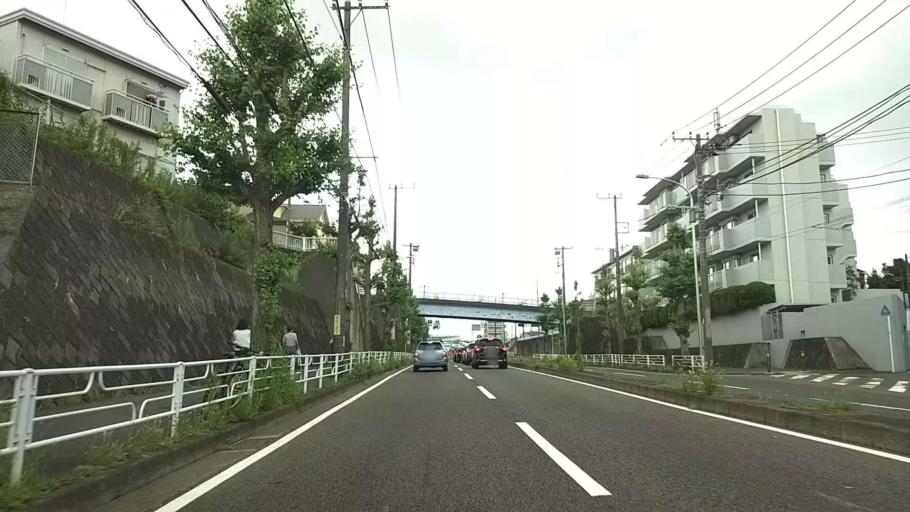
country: JP
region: Kanagawa
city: Yokohama
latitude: 35.4961
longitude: 139.6075
